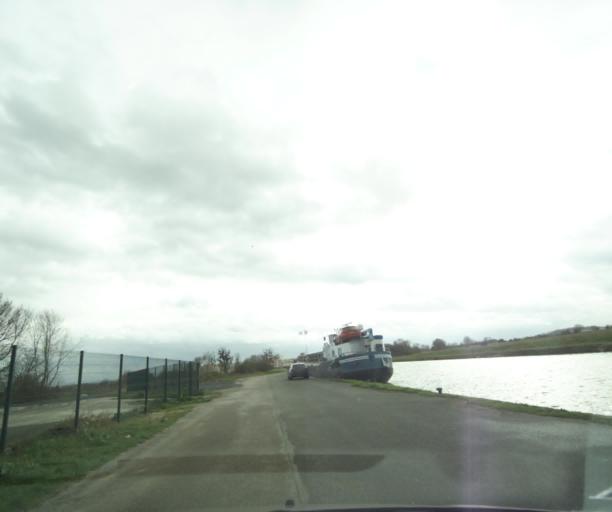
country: FR
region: Picardie
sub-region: Departement de l'Oise
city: Noyon
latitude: 49.5860
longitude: 2.9844
